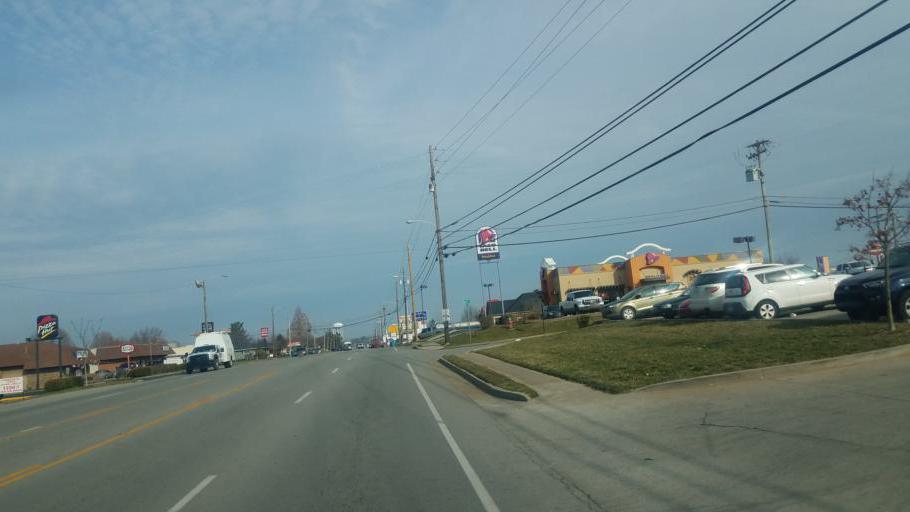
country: US
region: Kentucky
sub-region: Boyle County
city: Danville
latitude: 37.6200
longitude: -84.7745
